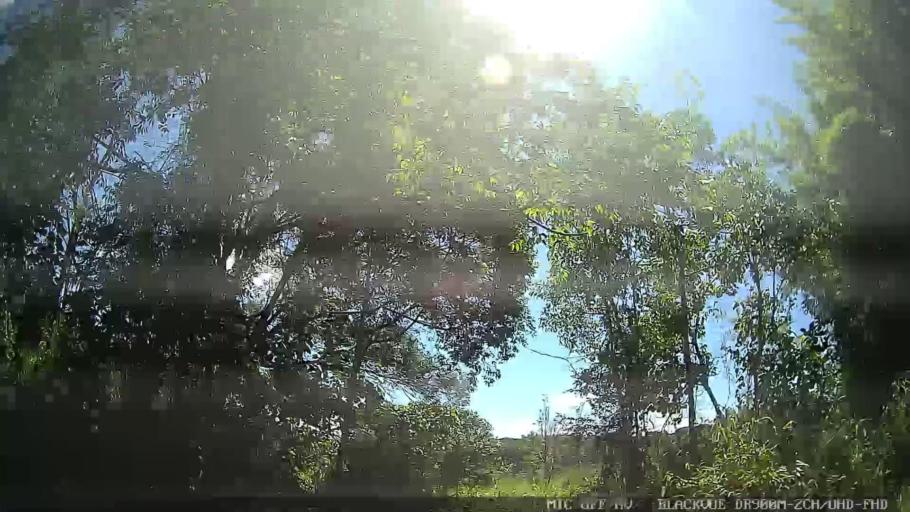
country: BR
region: Sao Paulo
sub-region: Mogi das Cruzes
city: Mogi das Cruzes
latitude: -23.5982
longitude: -46.1523
